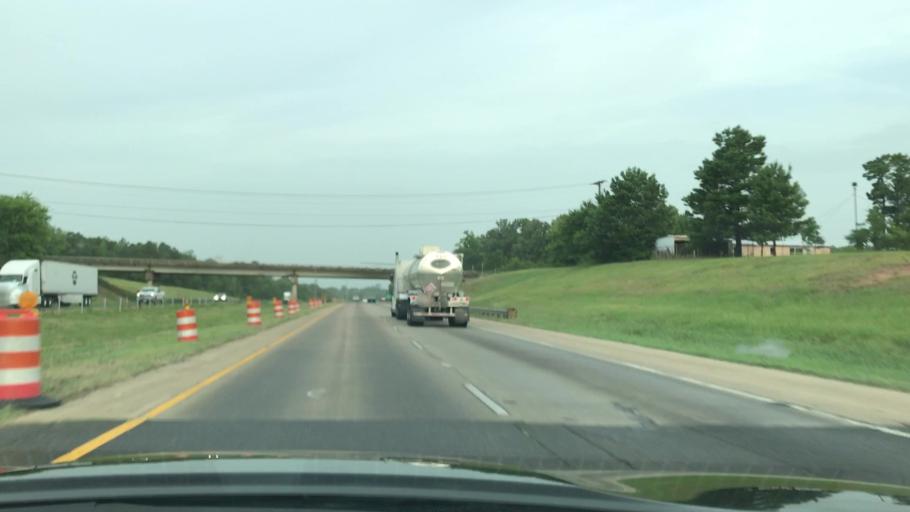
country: US
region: Louisiana
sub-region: Caddo Parish
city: Greenwood
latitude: 32.4518
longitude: -94.0096
